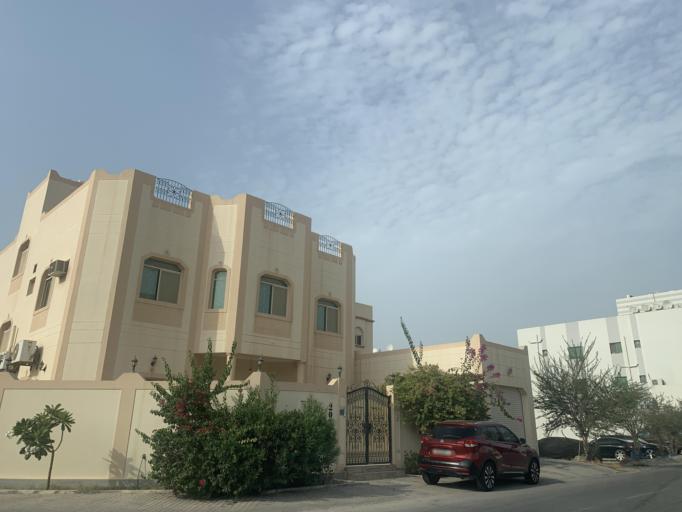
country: BH
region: Northern
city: Madinat `Isa
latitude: 26.1880
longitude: 50.4846
